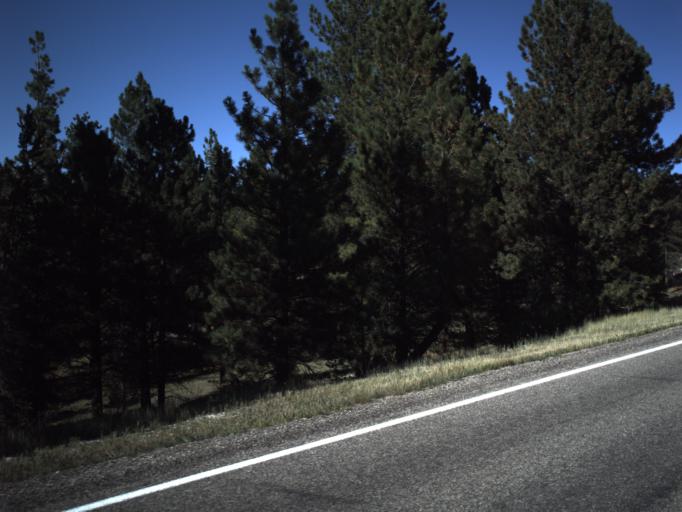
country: US
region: Utah
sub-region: Iron County
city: Parowan
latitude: 37.6998
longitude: -112.6591
